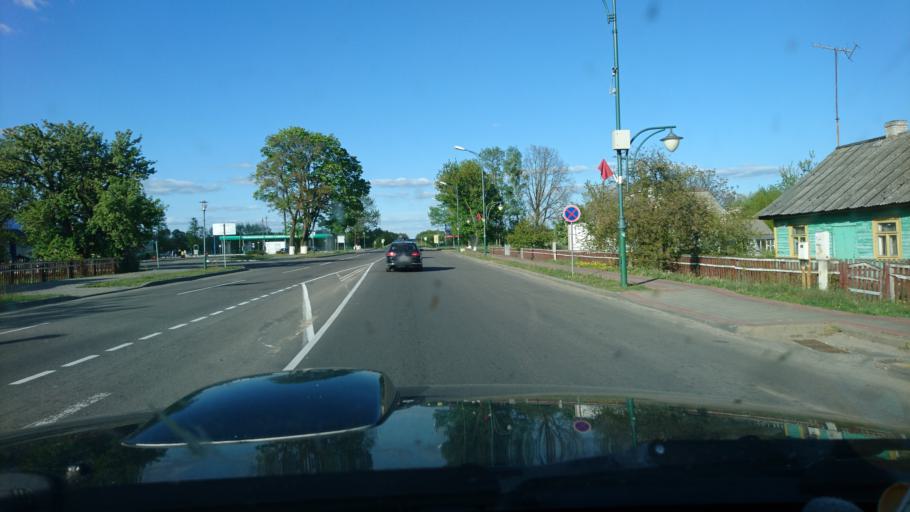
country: BY
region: Brest
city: Byaroza
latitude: 52.5394
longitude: 24.9950
